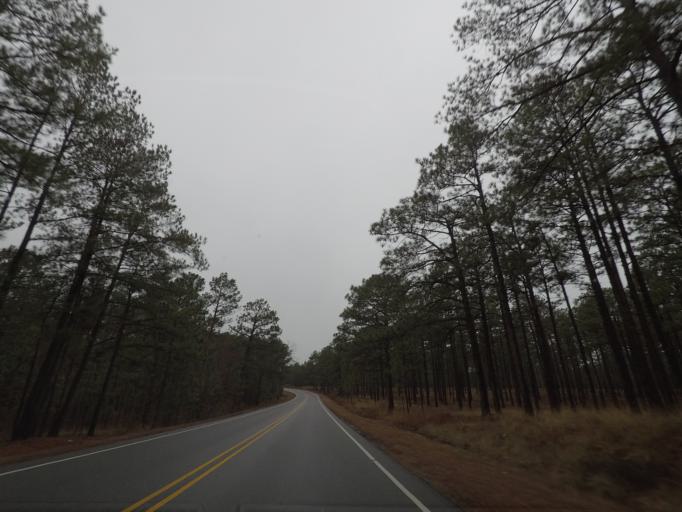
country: US
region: North Carolina
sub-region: Cumberland County
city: Spring Lake
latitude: 35.2340
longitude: -79.0134
